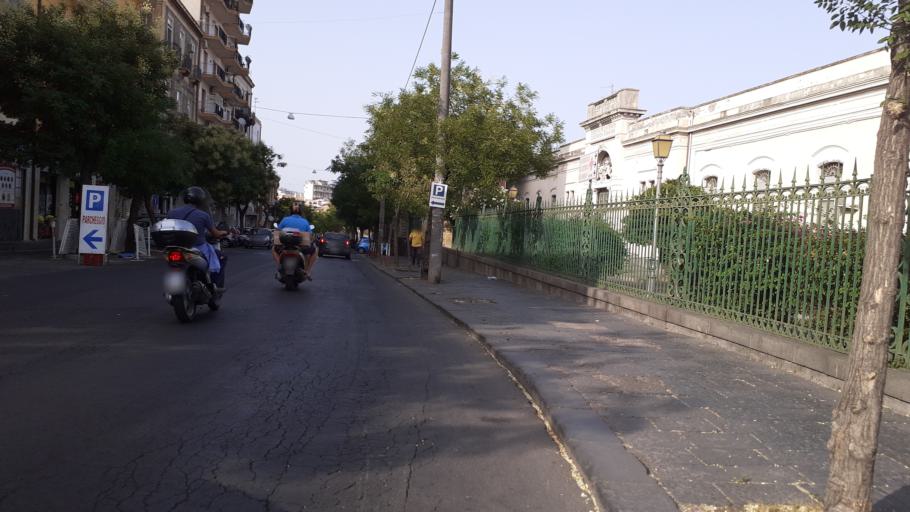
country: IT
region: Sicily
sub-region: Catania
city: Catania
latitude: 37.5047
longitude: 15.0773
